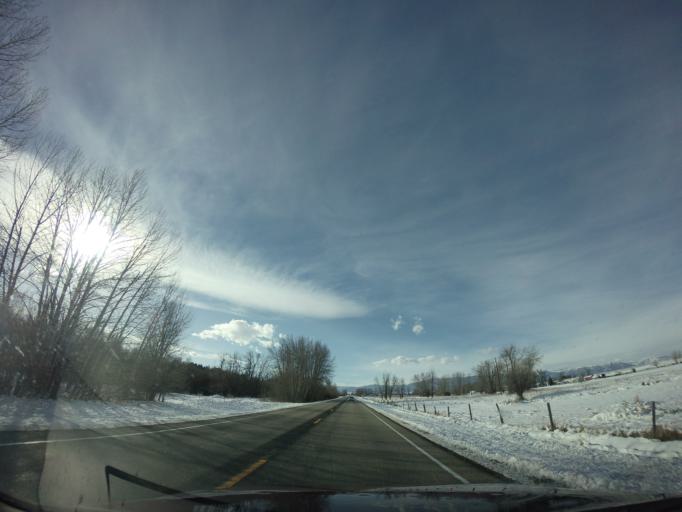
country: US
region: Montana
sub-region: Carbon County
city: Red Lodge
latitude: 45.3249
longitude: -109.1889
